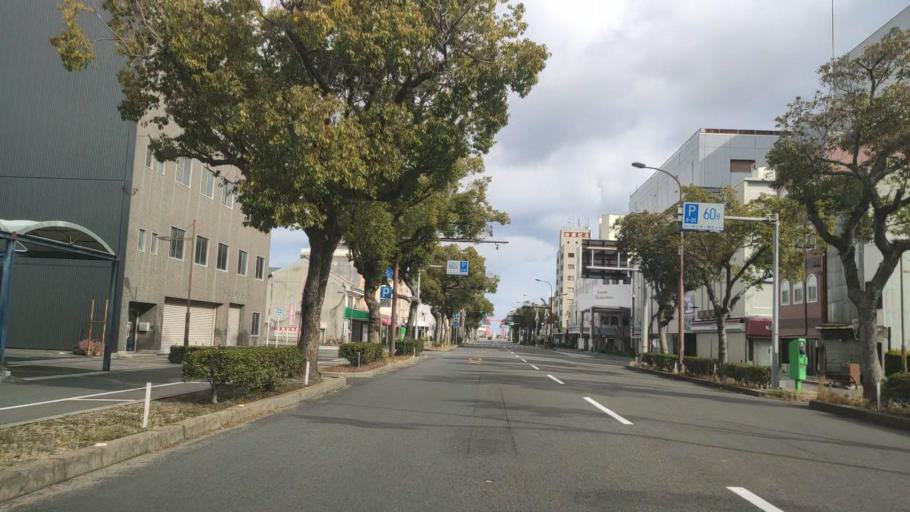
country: JP
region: Ehime
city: Saijo
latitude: 34.0684
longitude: 133.0013
